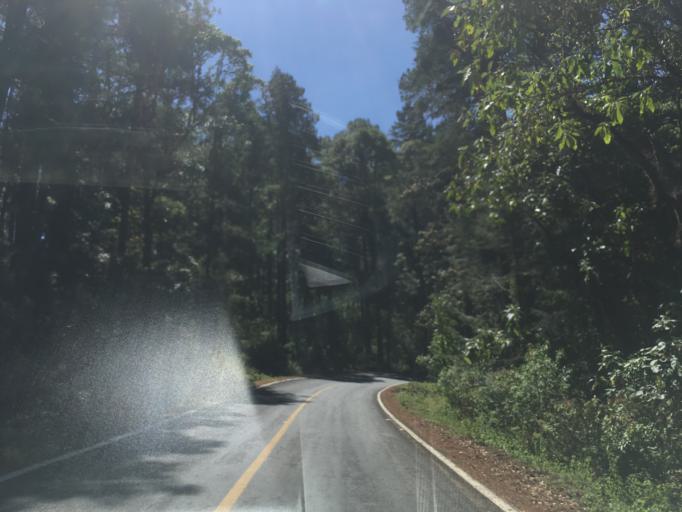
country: MX
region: Michoacan
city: Tzitzio
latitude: 19.6839
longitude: -100.8300
